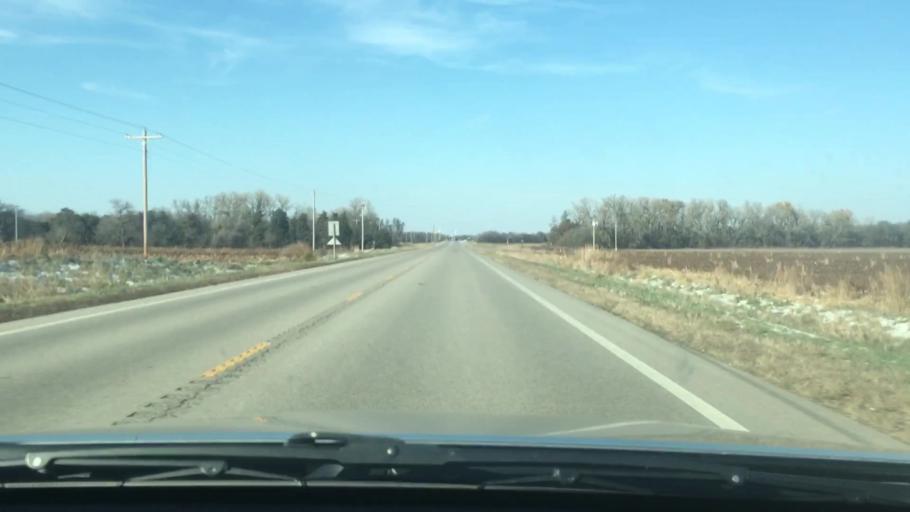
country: US
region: Kansas
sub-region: Rice County
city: Lyons
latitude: 38.3024
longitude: -98.2019
